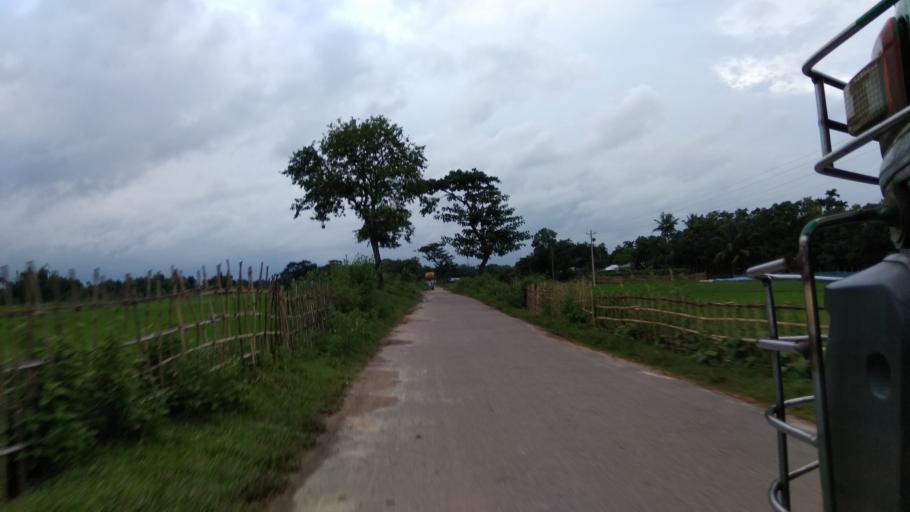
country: IN
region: Tripura
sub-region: Dhalai
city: Kamalpur
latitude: 24.2101
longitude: 91.8610
